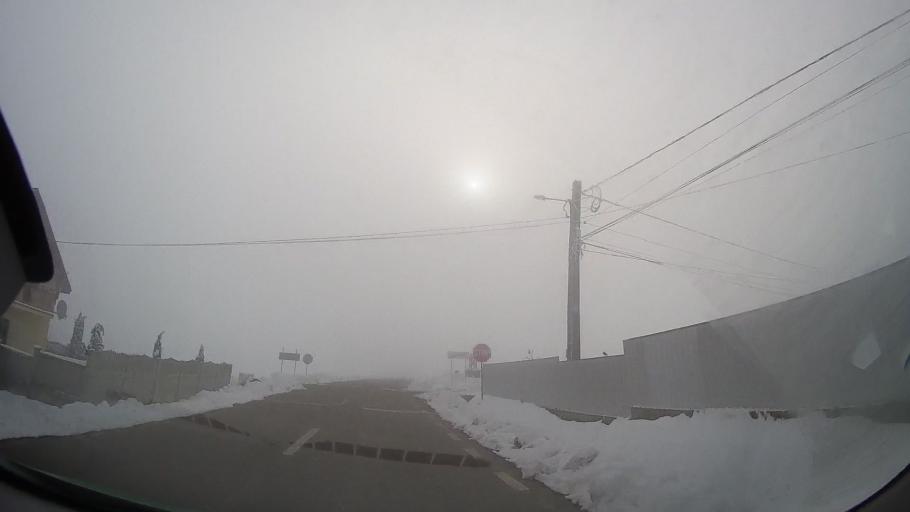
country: RO
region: Iasi
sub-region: Comuna Valea Seaca
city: Valea Seaca
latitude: 47.2808
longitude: 26.6703
